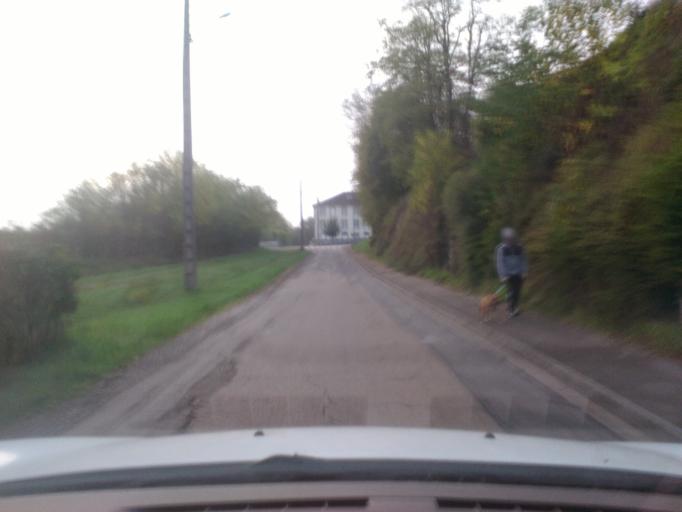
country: FR
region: Lorraine
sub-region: Departement des Vosges
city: Mirecourt
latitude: 48.2998
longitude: 6.1282
